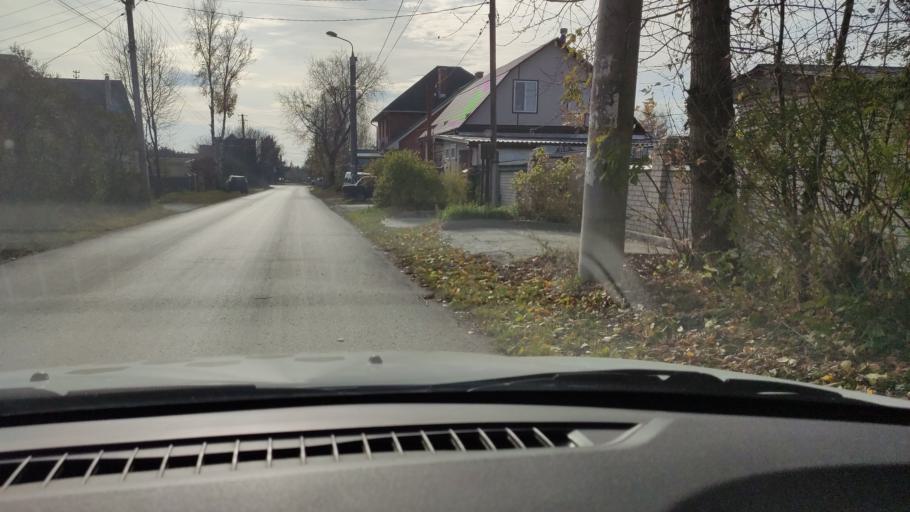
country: RU
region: Perm
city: Kondratovo
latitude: 58.0421
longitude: 56.1185
